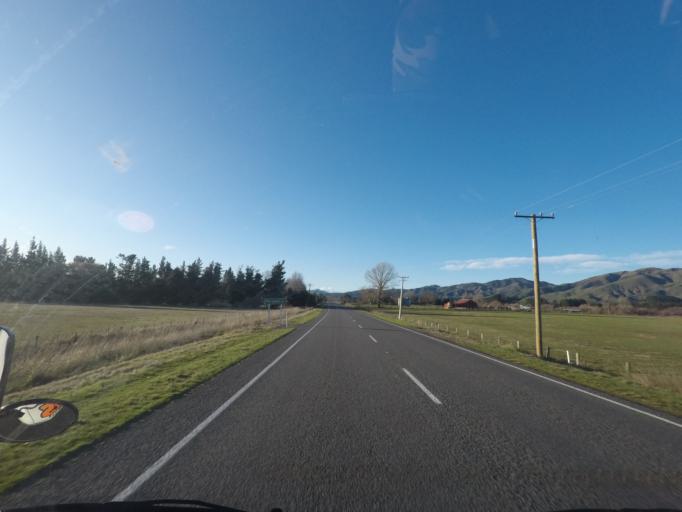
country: NZ
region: Canterbury
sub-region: Kaikoura District
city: Kaikoura
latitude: -42.7173
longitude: 173.2877
